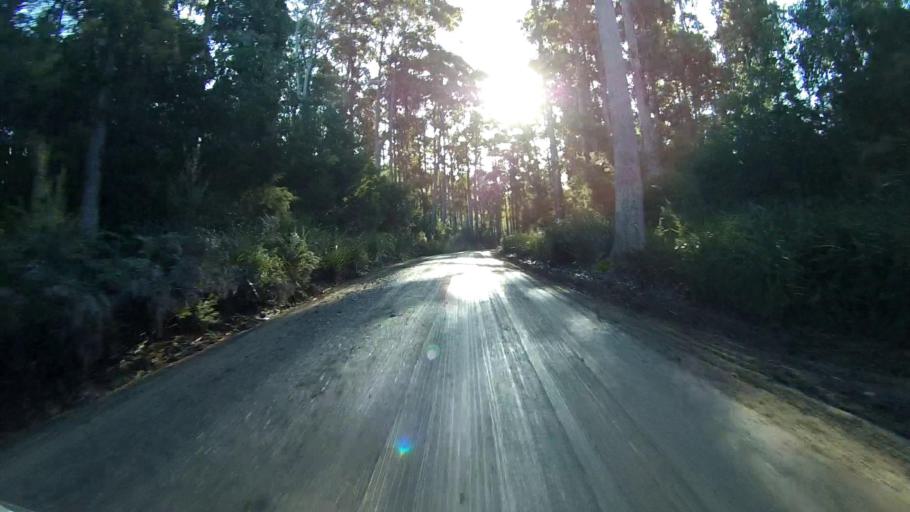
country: AU
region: Tasmania
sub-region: Clarence
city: Sandford
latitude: -43.1343
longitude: 147.9307
